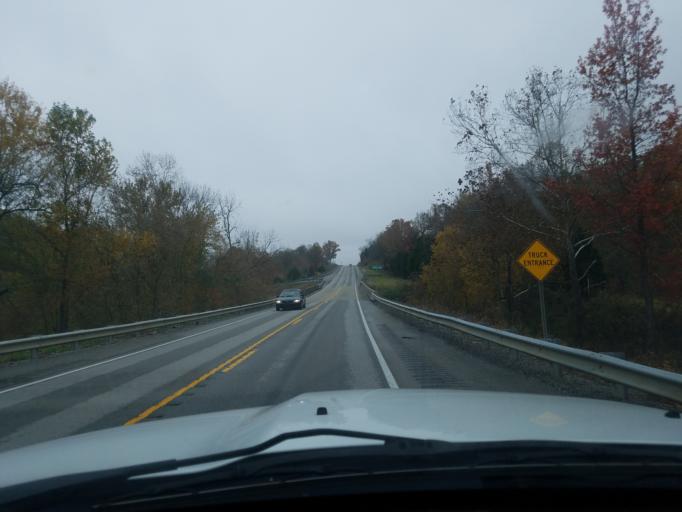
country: US
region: Kentucky
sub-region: Taylor County
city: Campbellsville
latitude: 37.3956
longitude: -85.4688
